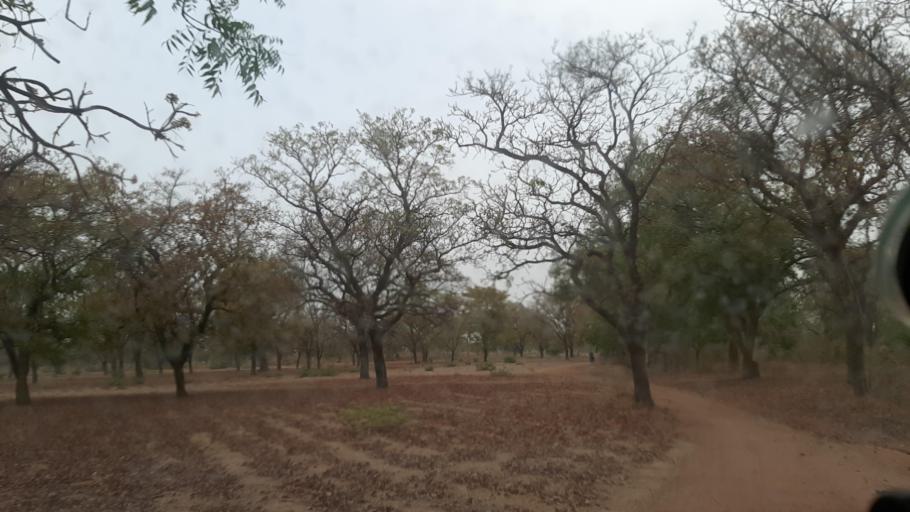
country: BF
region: Boucle du Mouhoun
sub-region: Province des Banwa
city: Salanso
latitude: 11.8507
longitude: -4.4261
